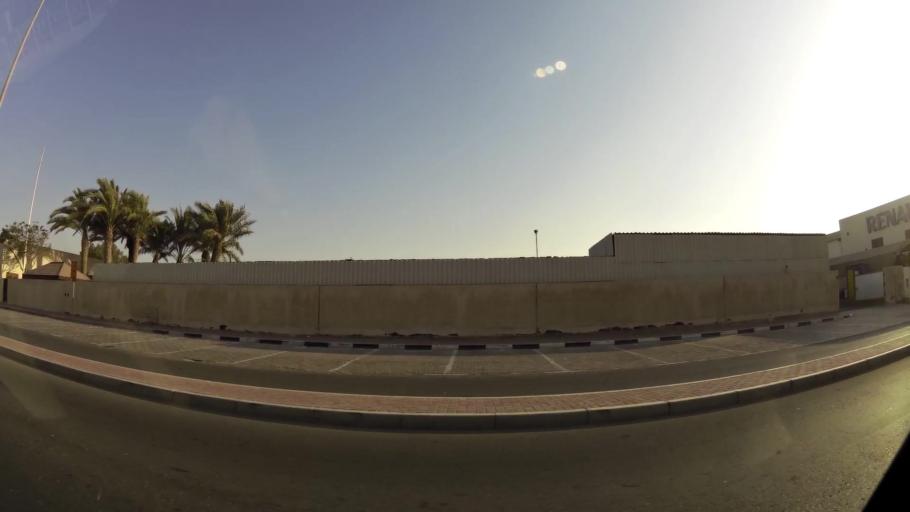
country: AE
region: Dubai
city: Dubai
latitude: 25.1539
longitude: 55.2317
